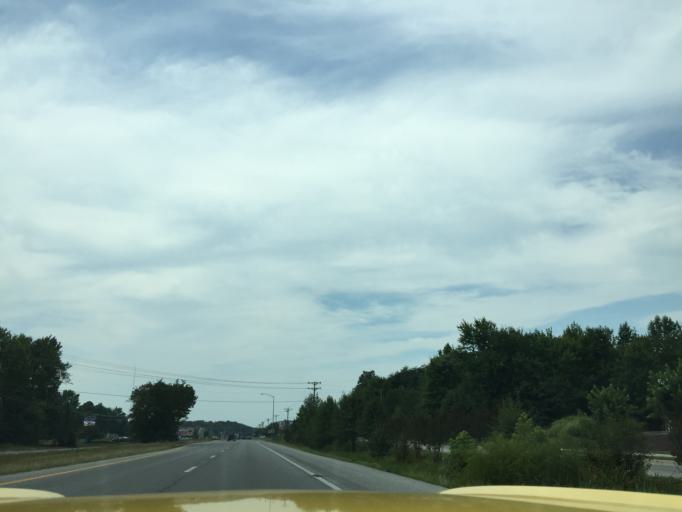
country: US
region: Maryland
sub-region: Charles County
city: Bryans Road
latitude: 38.6303
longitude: -77.0665
